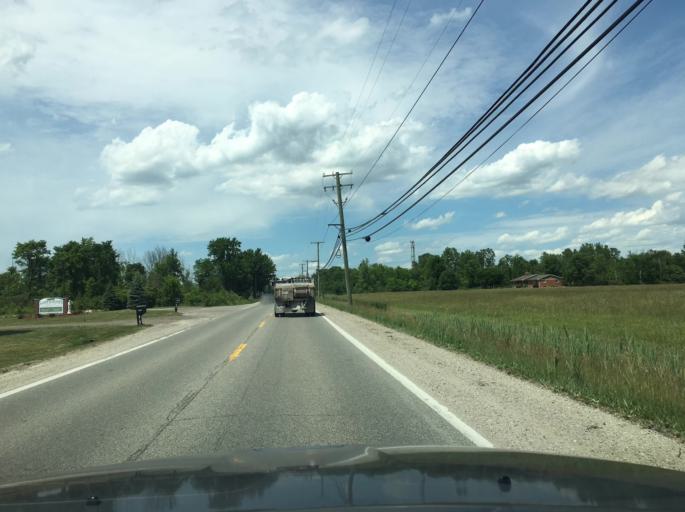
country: US
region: Michigan
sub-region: Macomb County
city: Shelby
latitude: 42.7195
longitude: -82.9596
